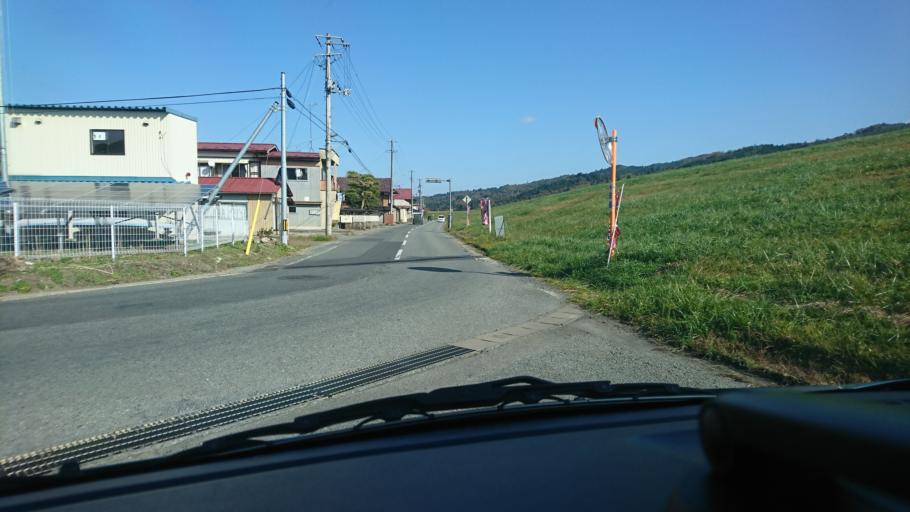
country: JP
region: Iwate
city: Ichinoseki
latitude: 38.8301
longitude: 141.2537
